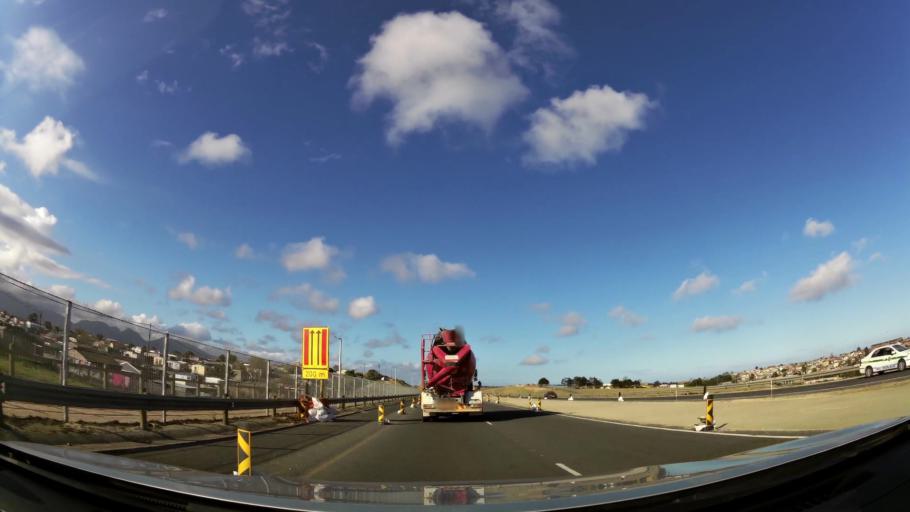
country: ZA
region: Western Cape
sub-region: Eden District Municipality
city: George
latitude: -33.9954
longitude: 22.4828
